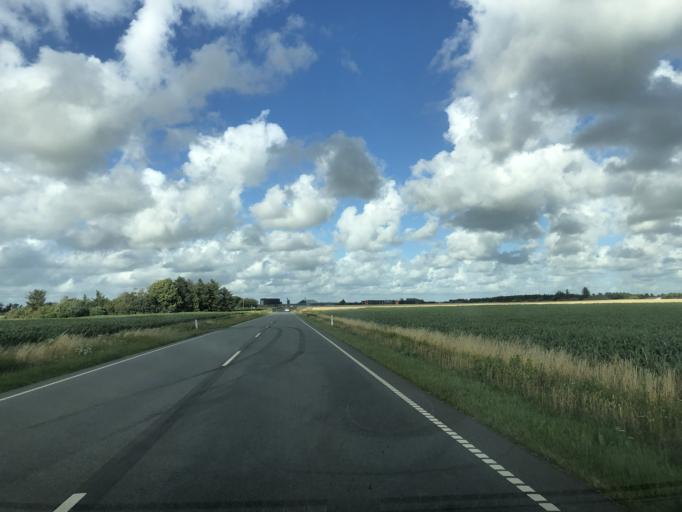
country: DK
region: Central Jutland
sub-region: Lemvig Kommune
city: Lemvig
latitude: 56.5092
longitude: 8.2923
